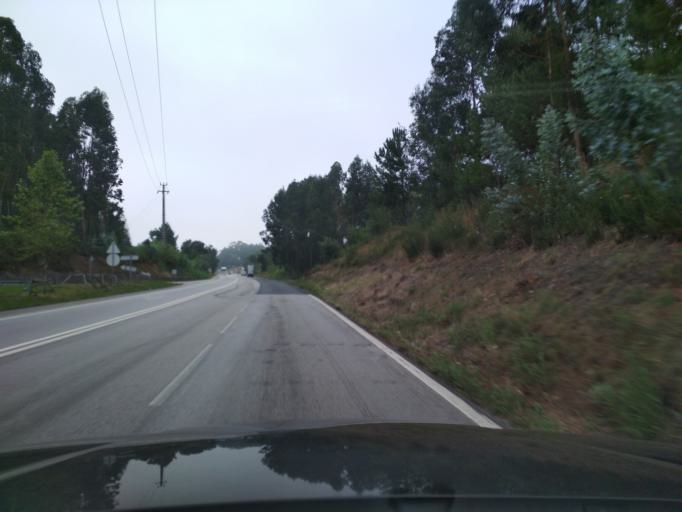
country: PT
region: Aveiro
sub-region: Mealhada
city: Pampilhosa do Botao
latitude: 40.2975
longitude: -8.4462
